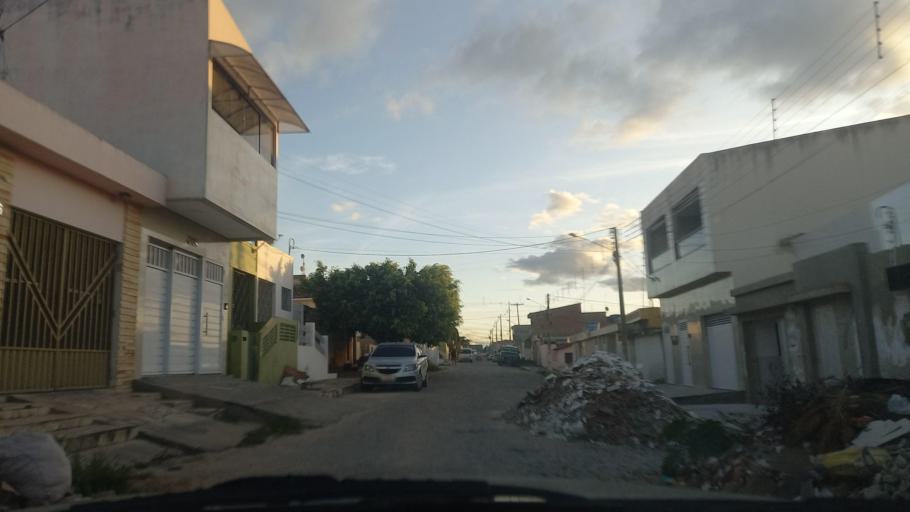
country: BR
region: Pernambuco
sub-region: Bezerros
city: Bezerros
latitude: -8.2388
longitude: -35.7488
